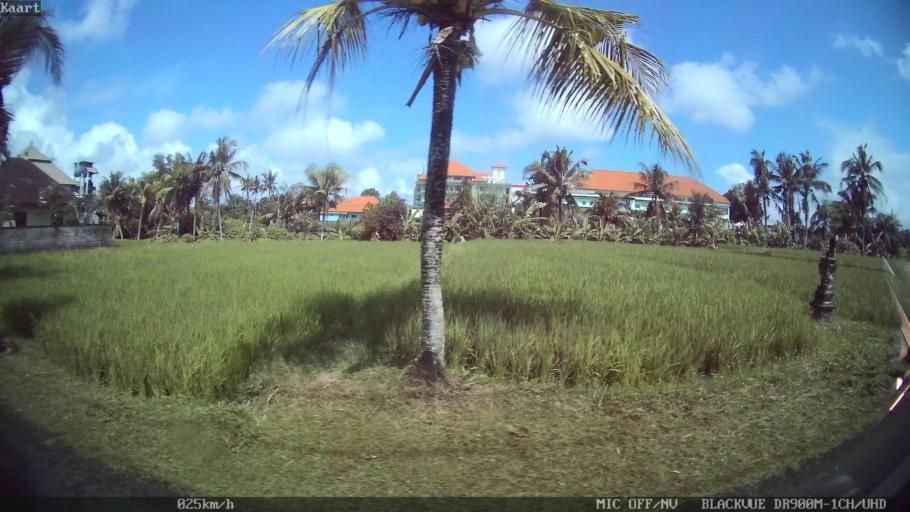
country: ID
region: Bali
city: Banjar Tebongkang
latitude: -8.5524
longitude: 115.2749
